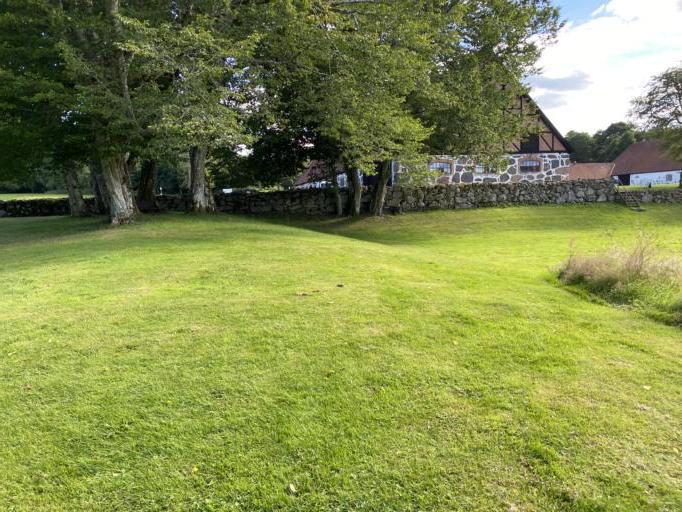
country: SE
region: Skane
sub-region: Hassleholms Kommun
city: Tormestorp
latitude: 56.1047
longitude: 13.7139
